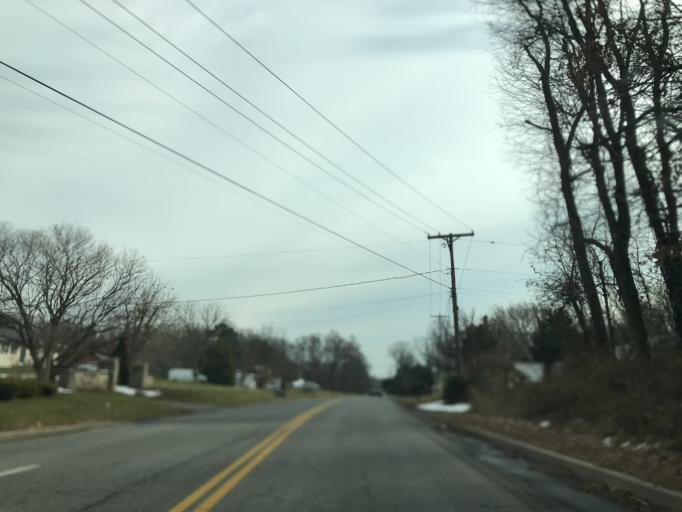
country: US
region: Maryland
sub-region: Harford County
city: Perryman
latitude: 39.4827
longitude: -76.2096
